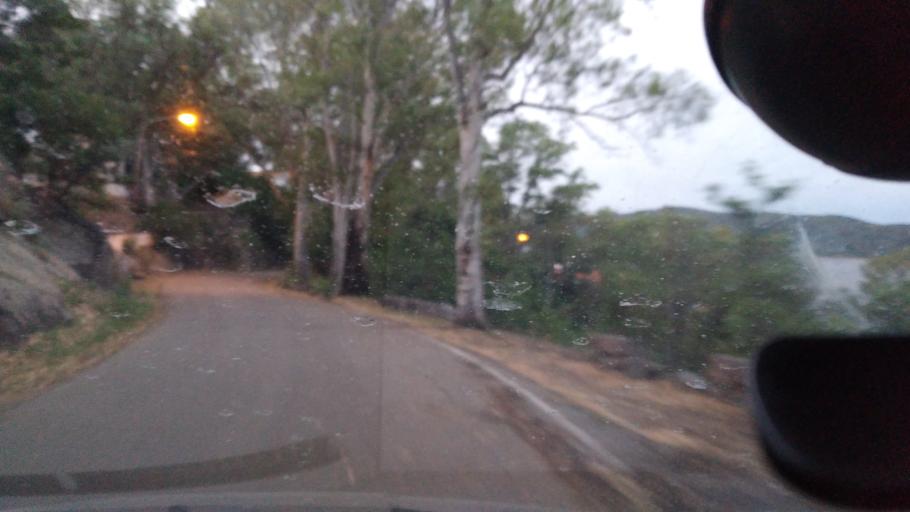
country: AR
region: Cordoba
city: Villa Las Rosas
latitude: -31.8727
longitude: -65.0320
